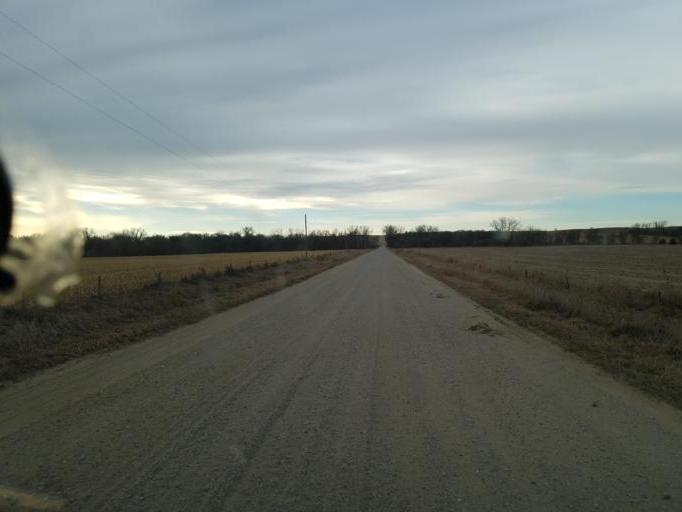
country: US
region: Nebraska
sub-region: Knox County
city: Bloomfield
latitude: 42.5555
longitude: -97.7596
